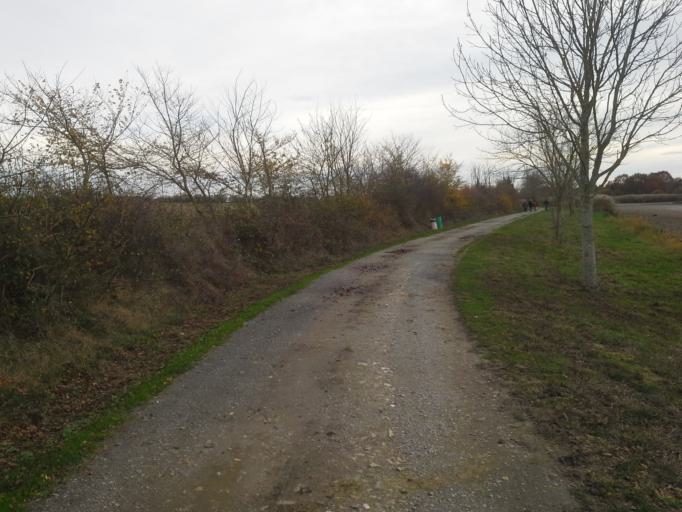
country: FR
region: Poitou-Charentes
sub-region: Departement de la Vienne
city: Pleumartin
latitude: 46.6356
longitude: 0.7655
